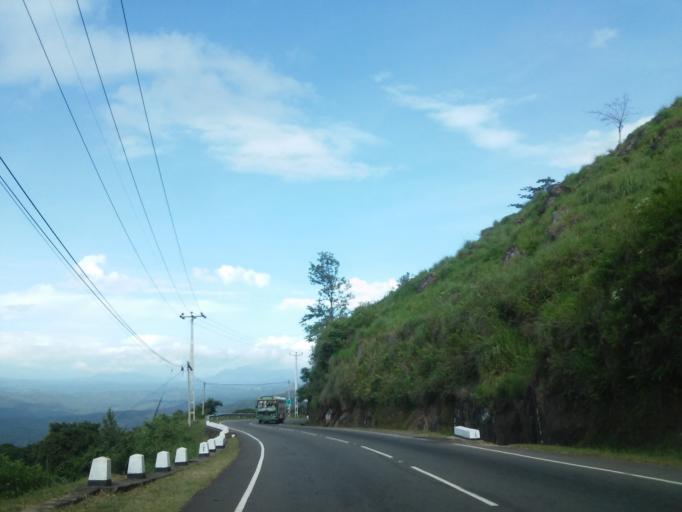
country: LK
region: Uva
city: Haputale
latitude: 6.7640
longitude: 80.9171
